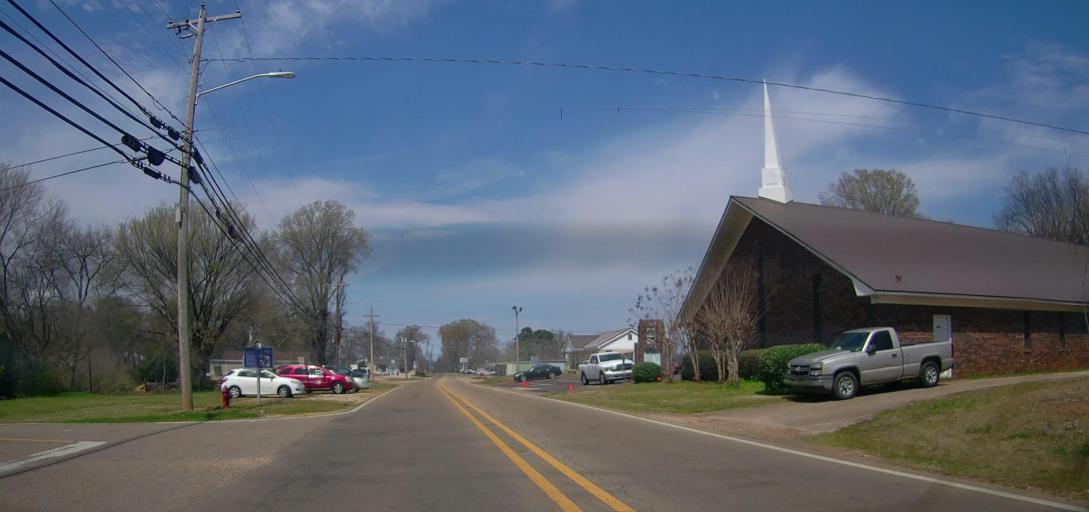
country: US
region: Mississippi
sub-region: Union County
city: New Albany
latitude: 34.4863
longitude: -89.0018
